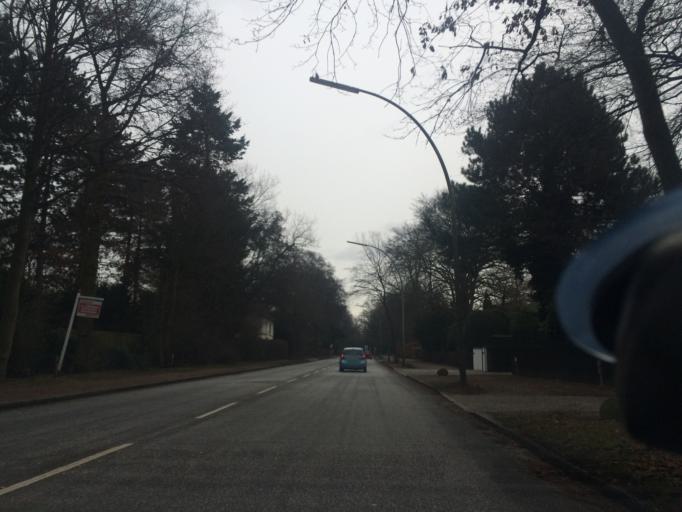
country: DE
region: Hamburg
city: Altona
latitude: 53.5466
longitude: 9.8842
